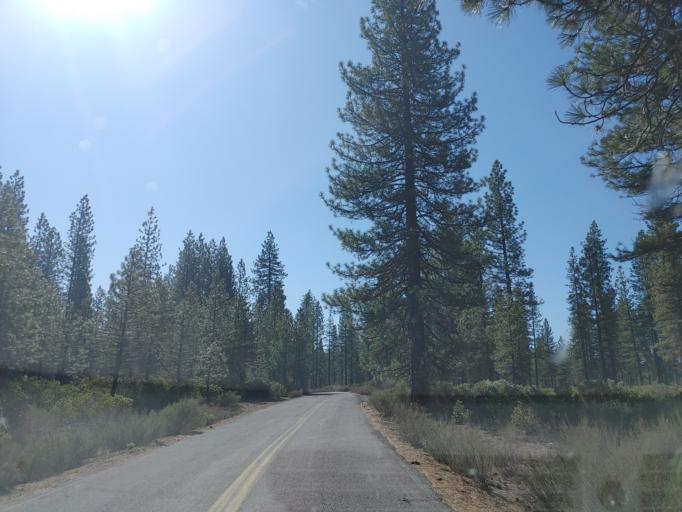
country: US
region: California
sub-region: Siskiyou County
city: McCloud
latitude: 41.2515
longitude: -122.0281
